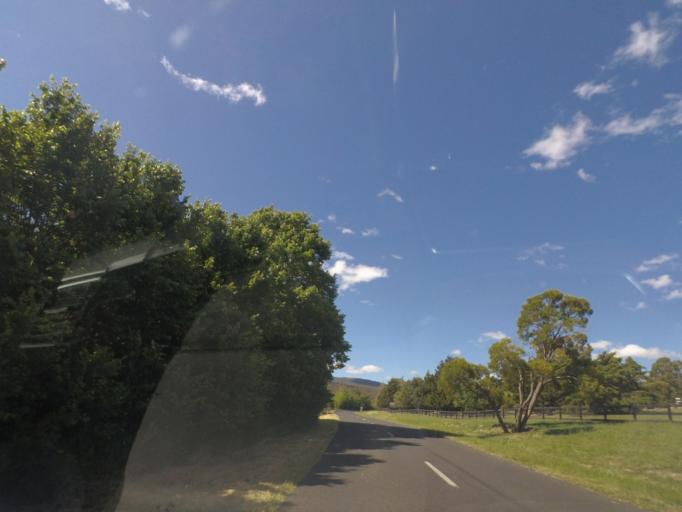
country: AU
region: Victoria
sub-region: Hume
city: Sunbury
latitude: -37.4319
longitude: 144.6089
